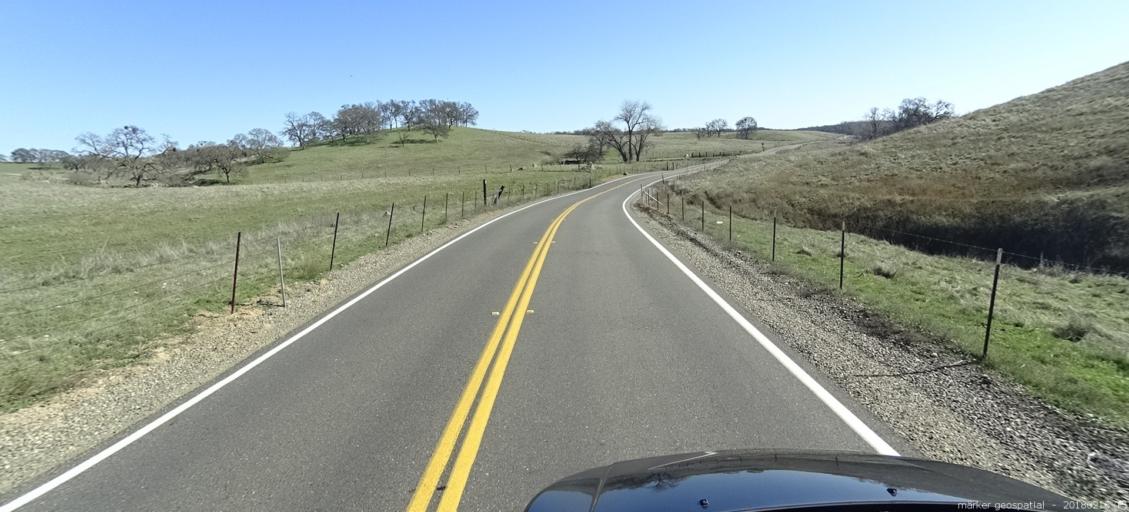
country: US
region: California
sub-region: Sacramento County
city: Rancho Murieta
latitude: 38.5559
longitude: -121.1168
